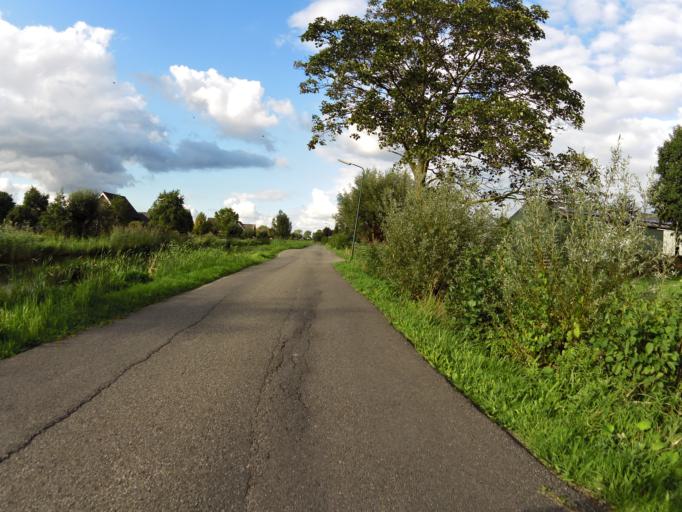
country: NL
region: Utrecht
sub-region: Gemeente Woerden
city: Woerden
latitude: 52.1306
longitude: 4.8938
